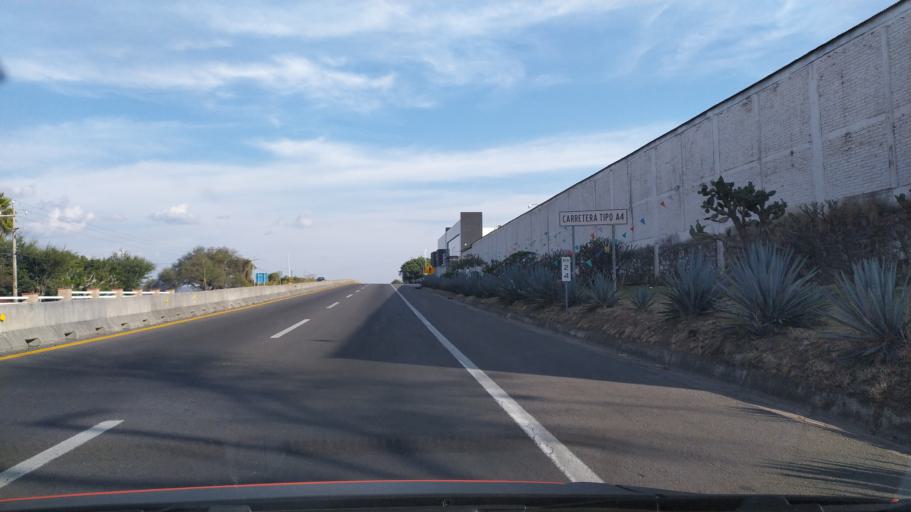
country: MX
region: Jalisco
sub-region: Poncitlan
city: El Romereno (INFONAVIT)
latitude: 20.3931
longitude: -103.0111
